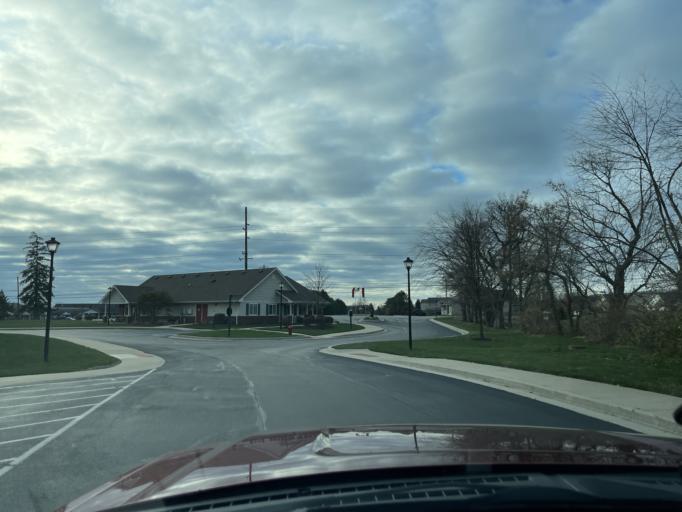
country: US
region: Indiana
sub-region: Hendricks County
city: Avon
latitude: 39.7629
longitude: -86.4630
